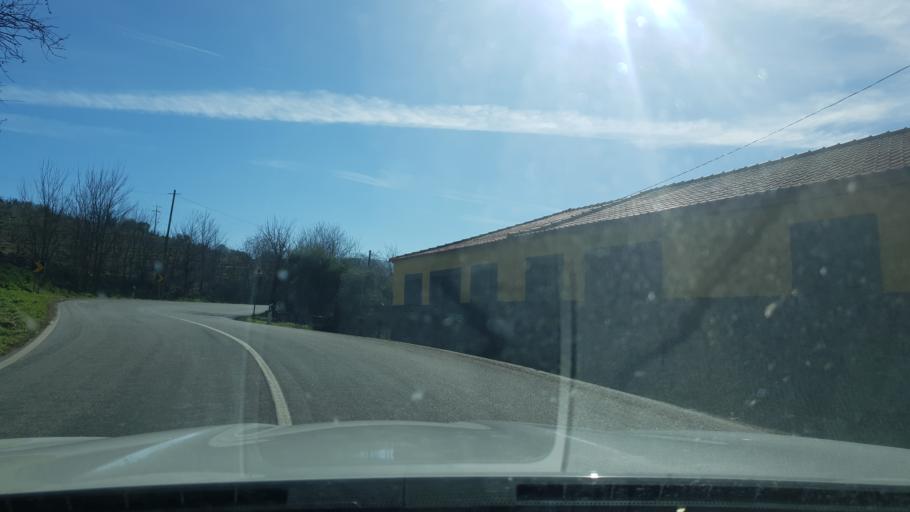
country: PT
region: Braganca
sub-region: Torre de Moncorvo
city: Torre de Moncorvo
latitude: 41.2157
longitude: -7.0922
